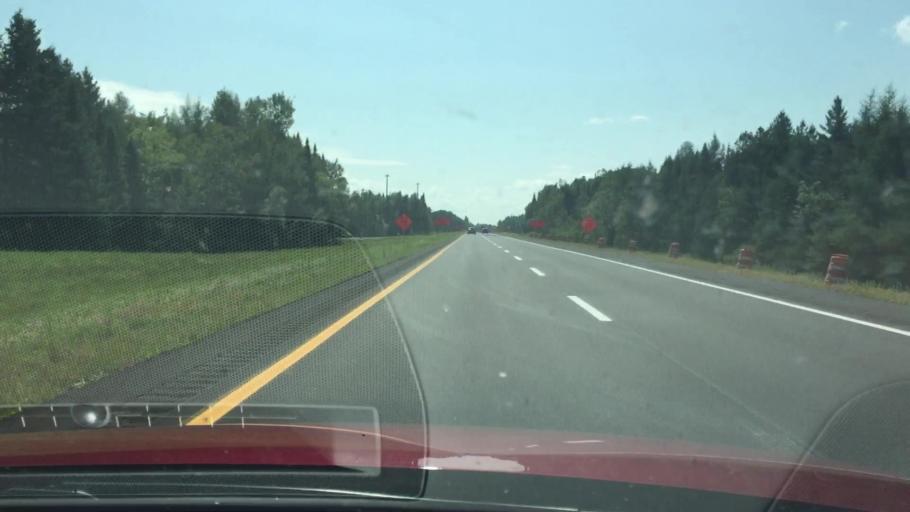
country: US
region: Maine
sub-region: Penobscot County
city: Patten
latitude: 45.8804
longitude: -68.4099
